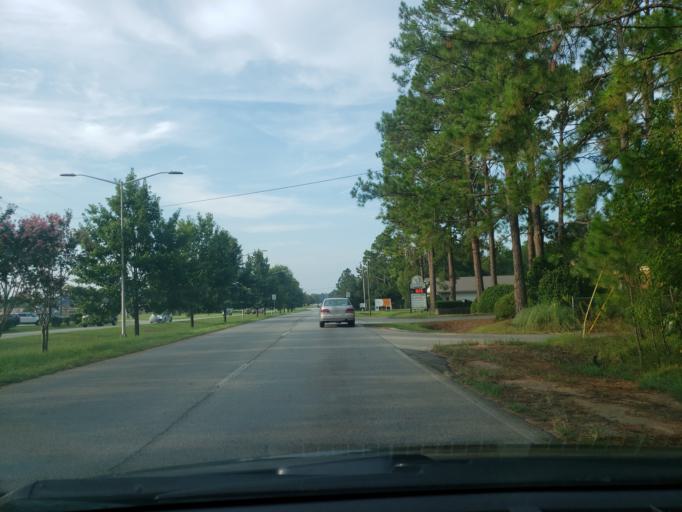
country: US
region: Georgia
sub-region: Dougherty County
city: Albany
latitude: 31.5903
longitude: -84.2196
